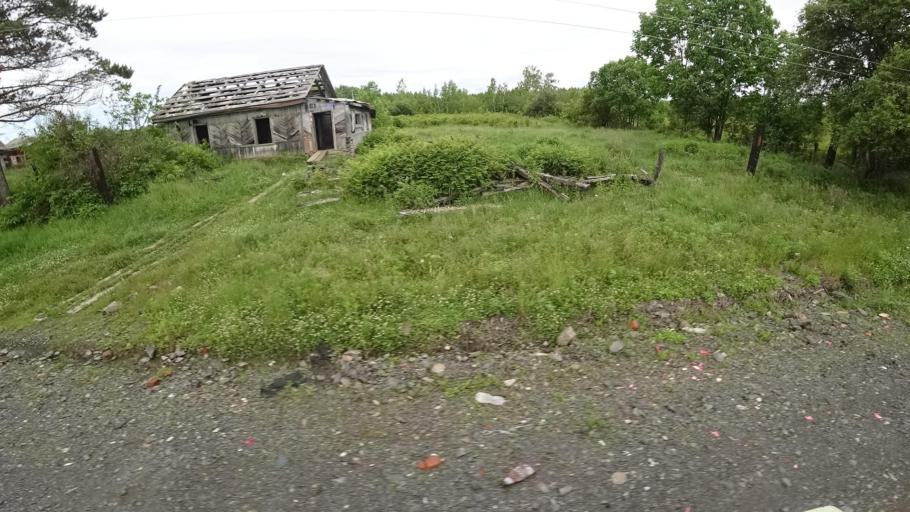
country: RU
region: Khabarovsk Krai
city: Amursk
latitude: 49.8882
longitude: 136.1288
